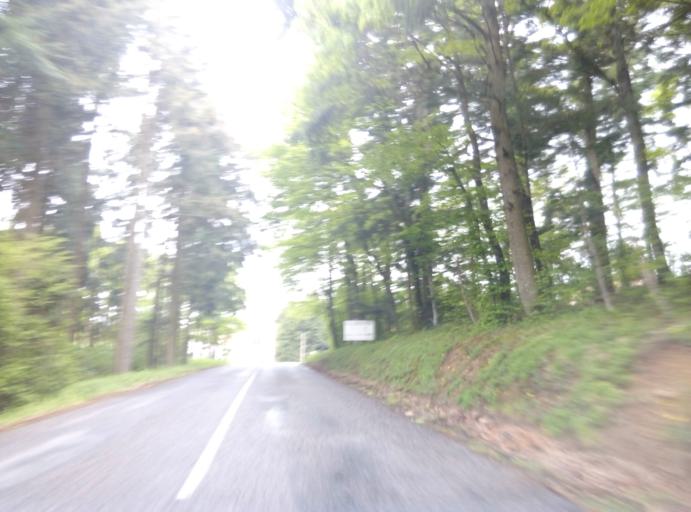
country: FR
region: Rhone-Alpes
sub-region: Departement du Rhone
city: Tarare
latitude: 45.9297
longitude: 4.4270
